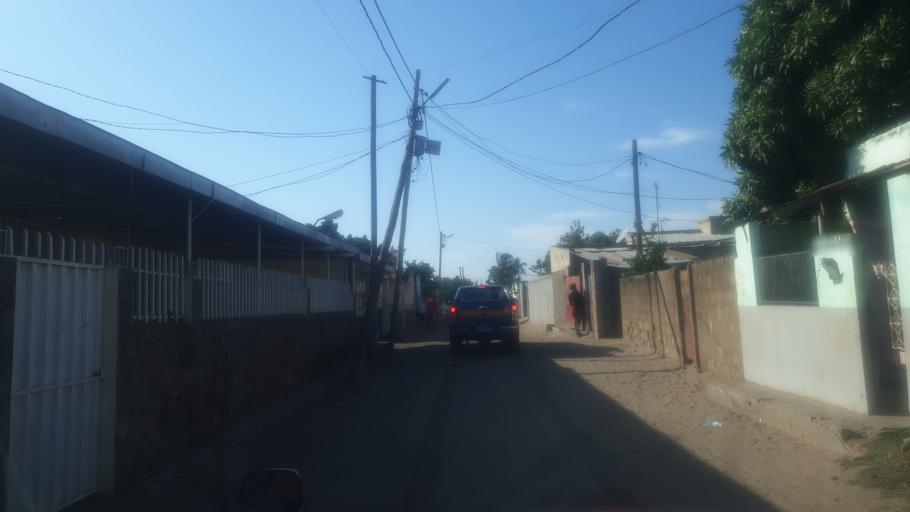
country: MZ
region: Maputo City
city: Maputo
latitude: -25.9128
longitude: 32.5611
